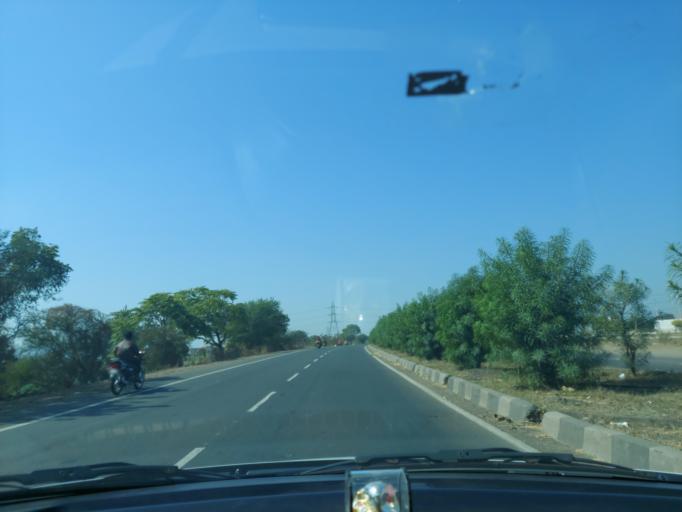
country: IN
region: Madhya Pradesh
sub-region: Indore
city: Manpur
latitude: 22.4234
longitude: 75.6064
